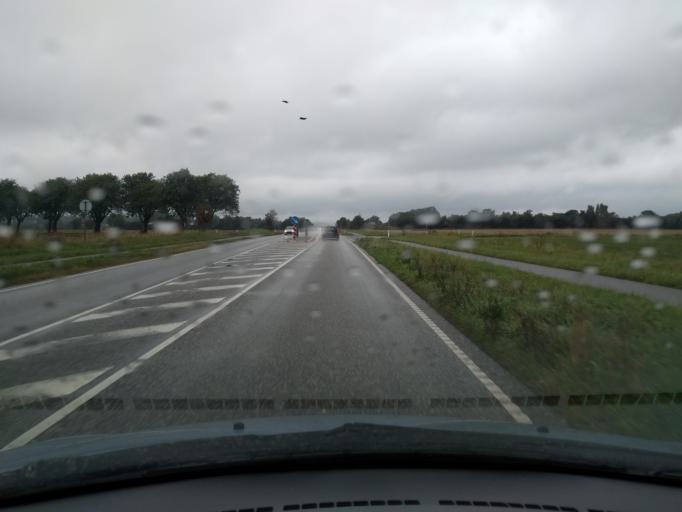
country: DK
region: Zealand
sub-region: Vordingborg Kommune
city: Neder Vindinge
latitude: 55.1071
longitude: 11.8211
